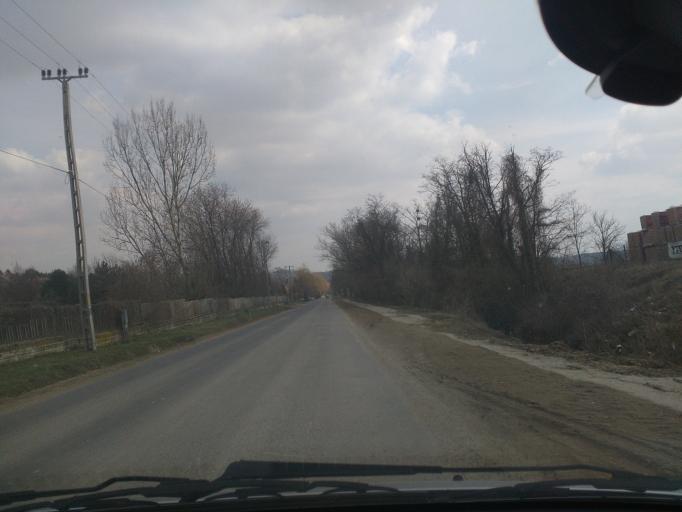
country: HU
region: Pest
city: Pilisborosjeno
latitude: 47.6028
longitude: 19.0009
